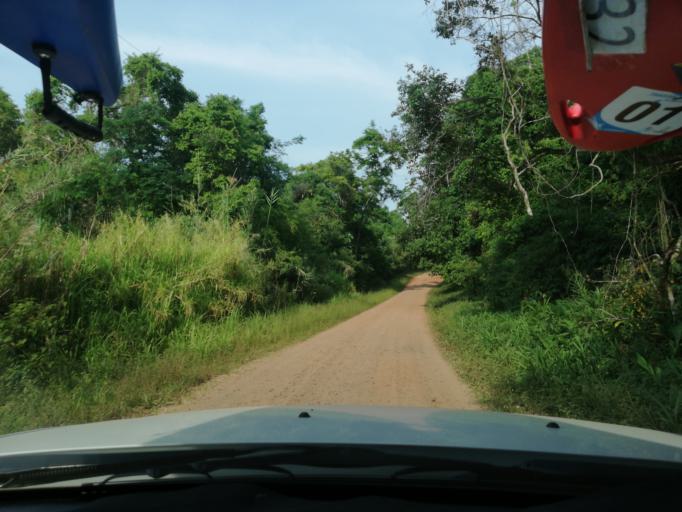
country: AR
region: Misiones
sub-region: Departamento de San Ignacio
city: San Ignacio
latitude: -27.3014
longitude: -55.5769
